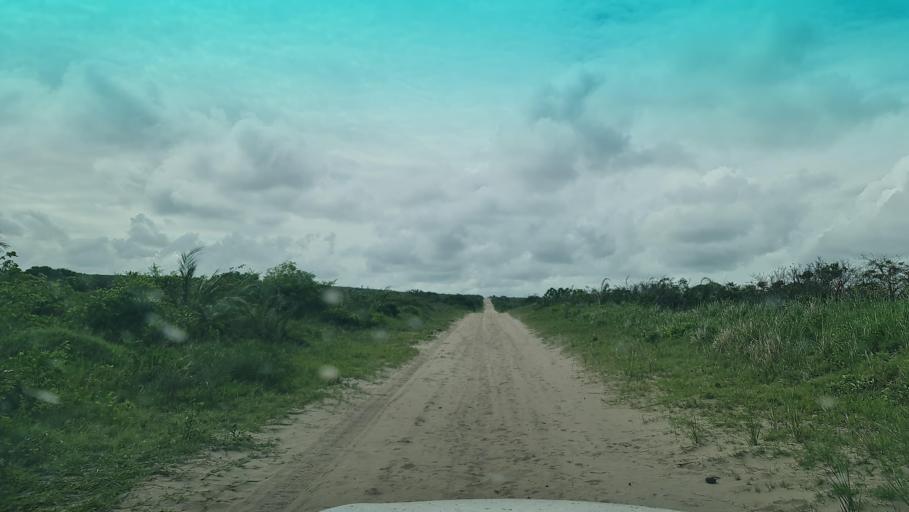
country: MZ
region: Maputo
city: Manhica
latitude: -25.4528
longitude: 32.9572
